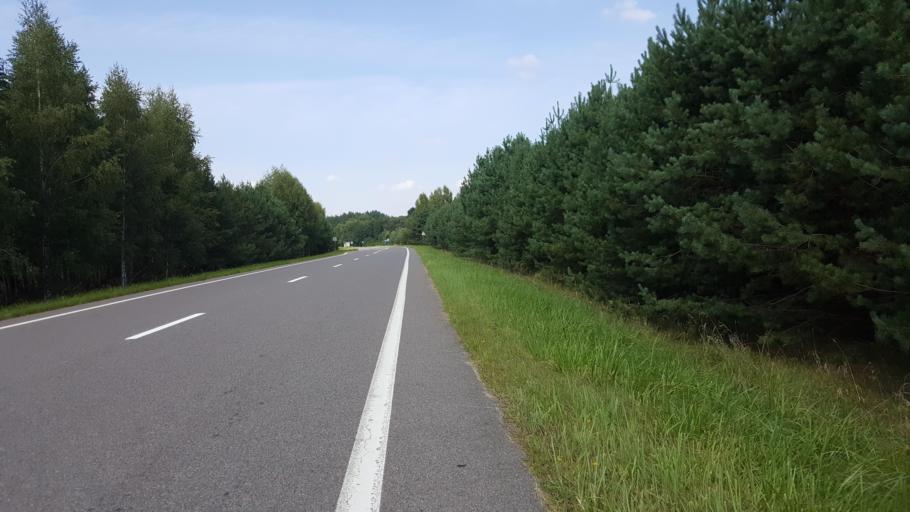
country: BY
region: Brest
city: Kamyanyuki
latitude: 52.5572
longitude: 23.6327
